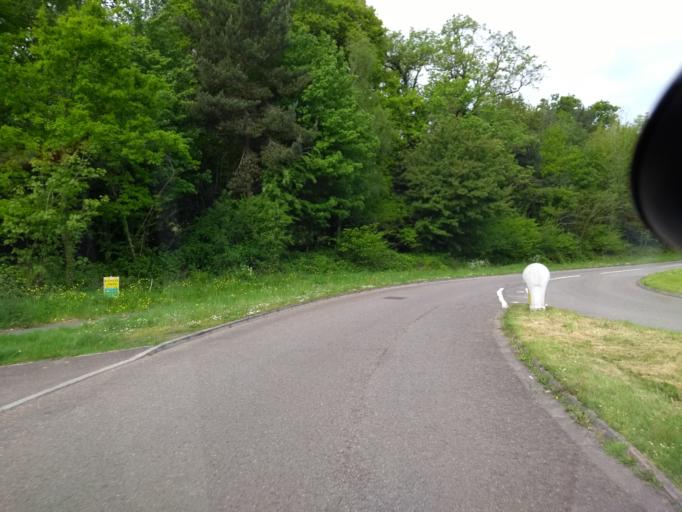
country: GB
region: England
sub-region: Dorset
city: Lyme Regis
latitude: 50.7408
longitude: -2.9149
